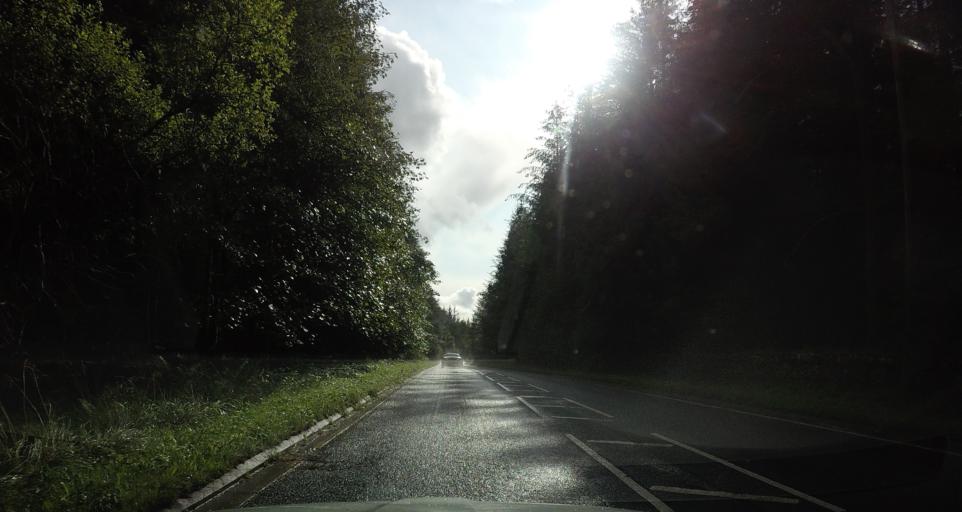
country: GB
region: Scotland
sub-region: Clackmannanshire
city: Dollar
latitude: 56.1249
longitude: -3.6898
